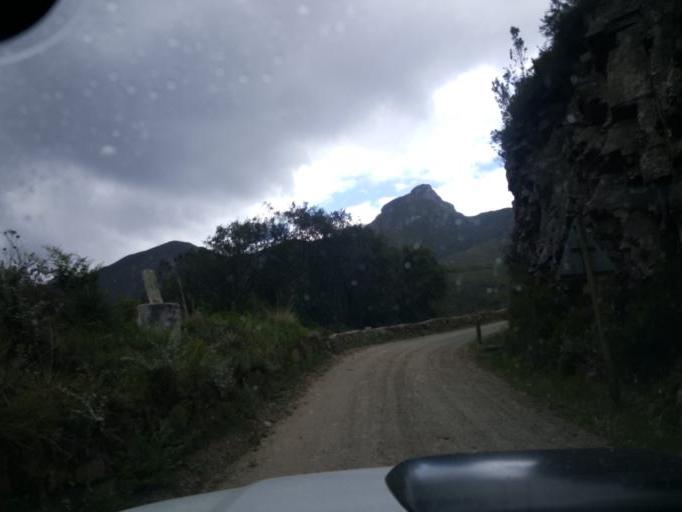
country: ZA
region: Western Cape
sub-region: Eden District Municipality
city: George
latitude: -33.8860
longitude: 22.4314
